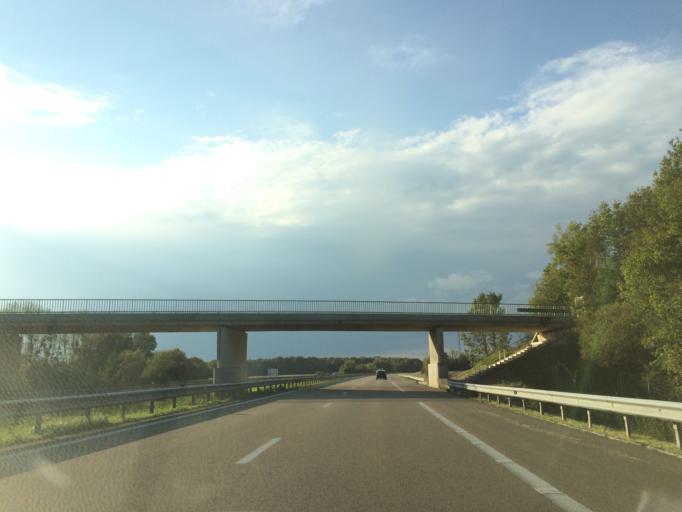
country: FR
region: Bourgogne
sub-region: Departement de l'Yonne
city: Cheroy
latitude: 48.1139
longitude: 2.9910
